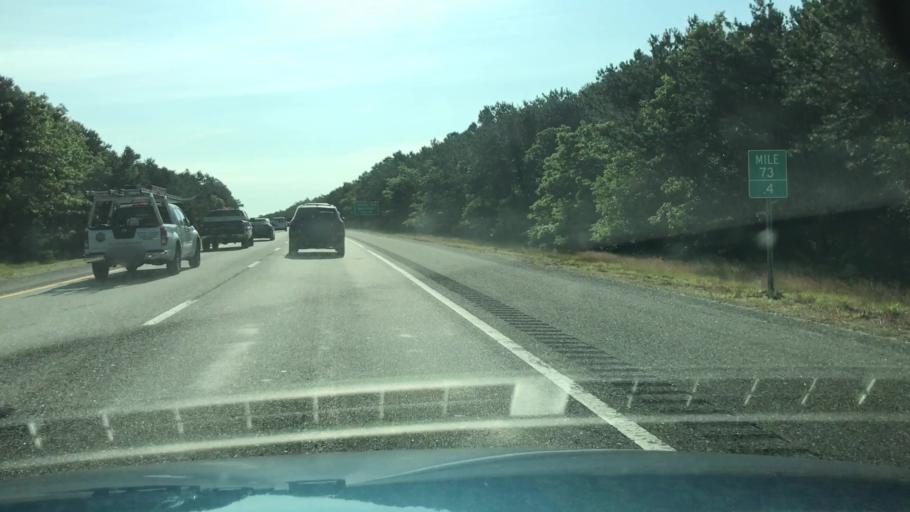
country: US
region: Massachusetts
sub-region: Barnstable County
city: Yarmouth Port
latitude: 41.6857
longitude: -70.2367
